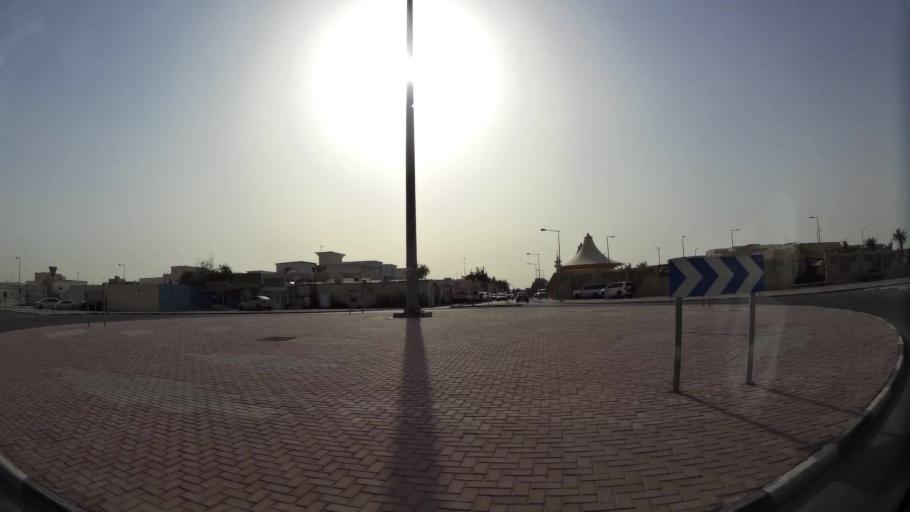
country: QA
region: Baladiyat ar Rayyan
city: Ar Rayyan
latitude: 25.2314
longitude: 51.4346
